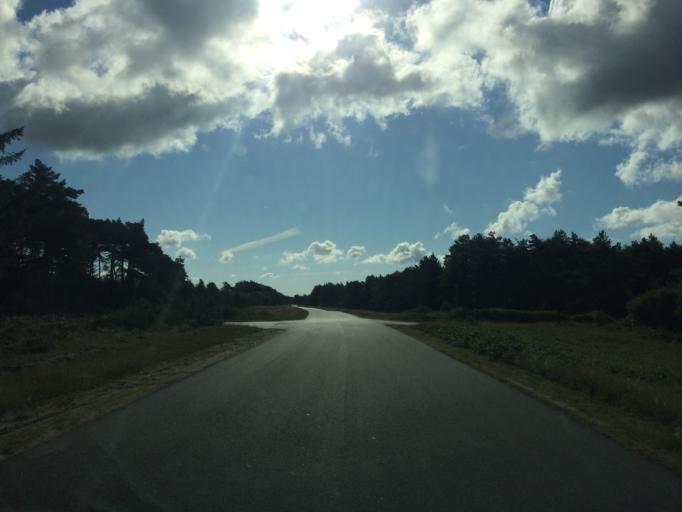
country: DK
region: South Denmark
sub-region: Varde Kommune
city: Oksbol
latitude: 55.6219
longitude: 8.2179
